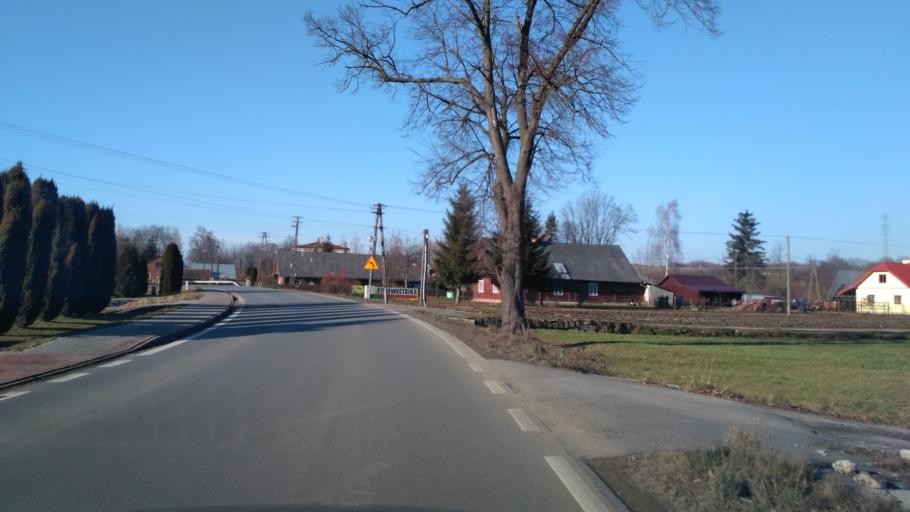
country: PL
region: Subcarpathian Voivodeship
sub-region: Powiat brzozowski
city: Haczow
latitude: 49.6785
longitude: 21.8693
